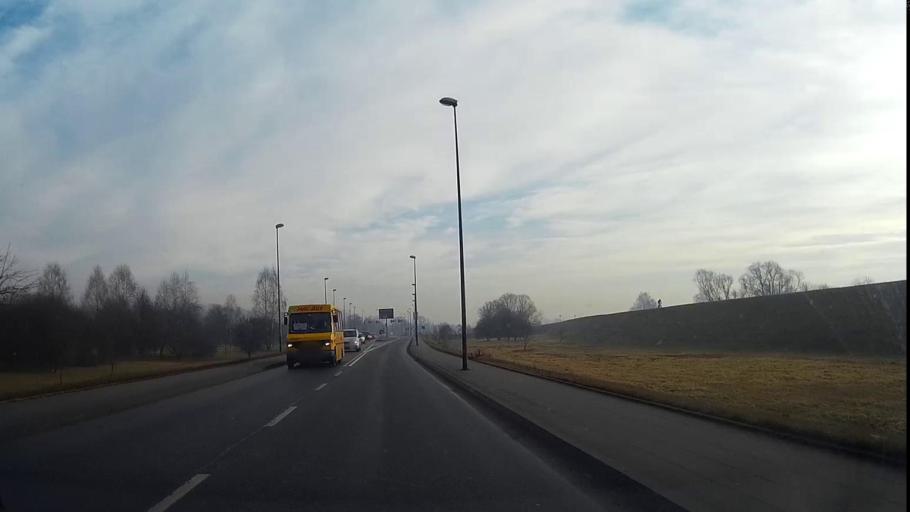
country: PL
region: Lesser Poland Voivodeship
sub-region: Powiat krakowski
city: Rzaska
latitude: 50.0459
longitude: 19.8686
